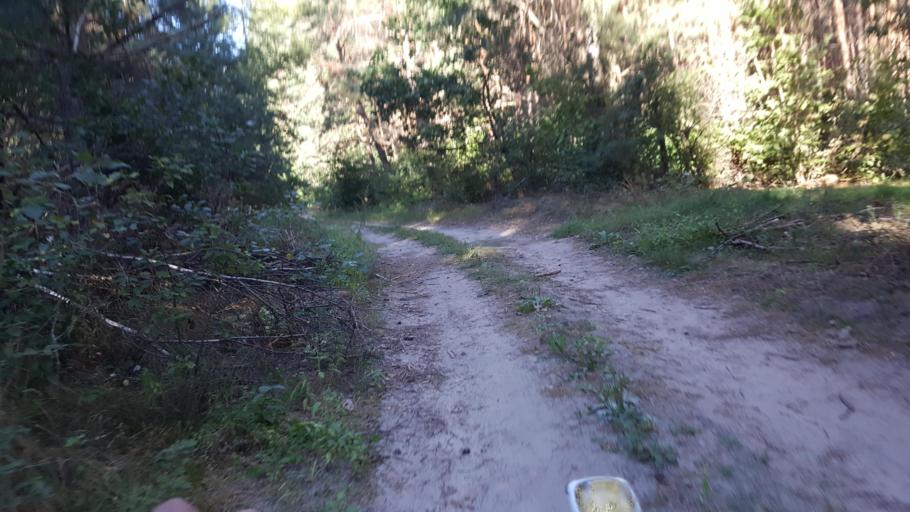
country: PL
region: Lublin Voivodeship
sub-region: Powiat bialski
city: Janow Podlaski
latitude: 52.3090
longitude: 23.2578
